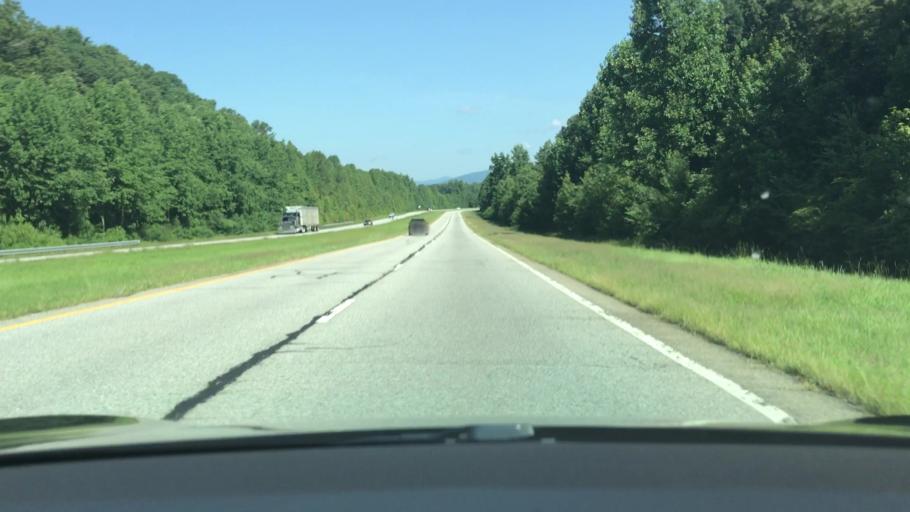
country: US
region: Georgia
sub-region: Habersham County
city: Clarkesville
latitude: 34.6022
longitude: -83.4450
